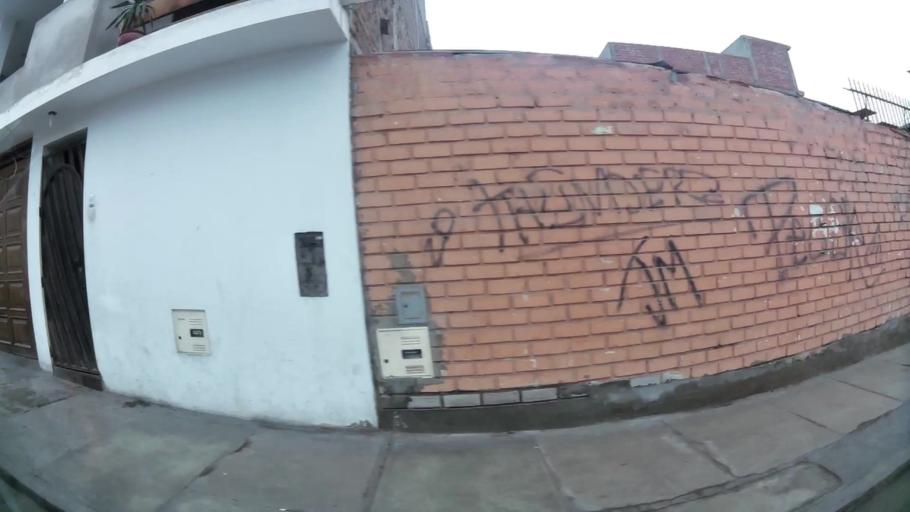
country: PE
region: Lima
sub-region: Lima
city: Surco
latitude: -12.1645
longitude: -76.9647
